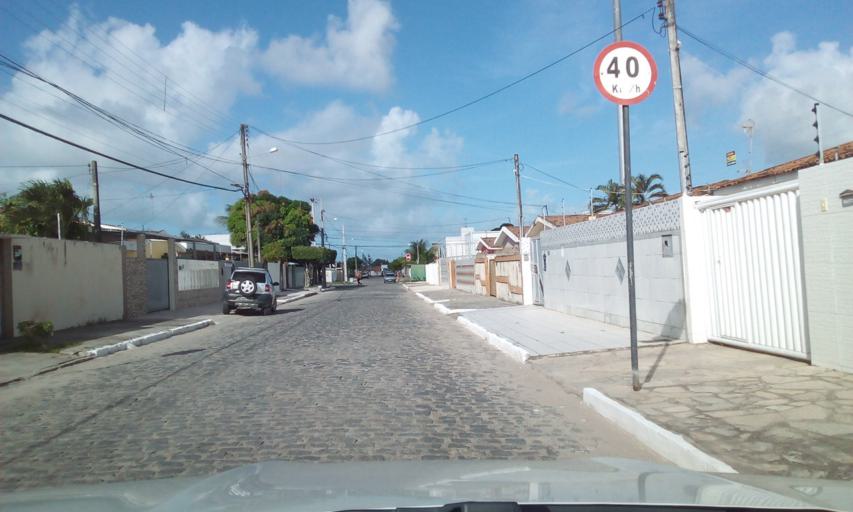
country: BR
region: Paraiba
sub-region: Joao Pessoa
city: Joao Pessoa
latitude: -7.1742
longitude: -34.8695
